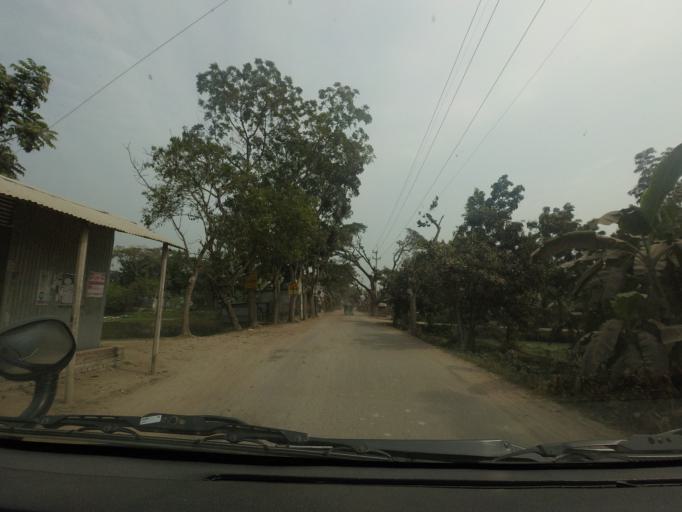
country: BD
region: Dhaka
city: Kishorganj
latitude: 24.3429
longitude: 90.7895
